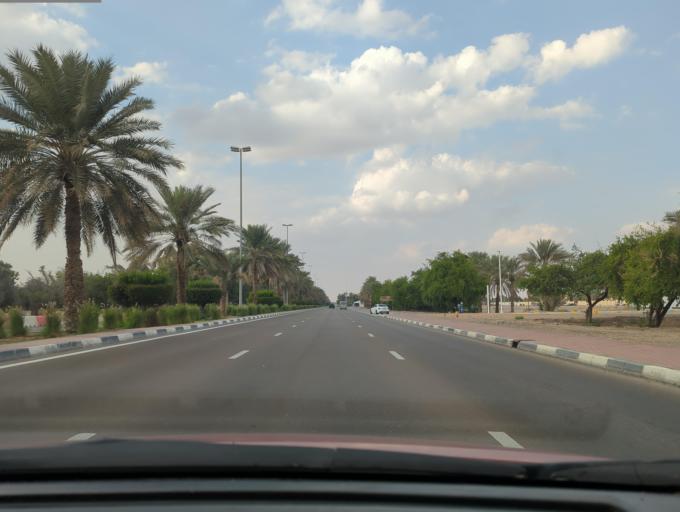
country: AE
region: Abu Dhabi
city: Al Ain
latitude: 24.1797
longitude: 55.6621
